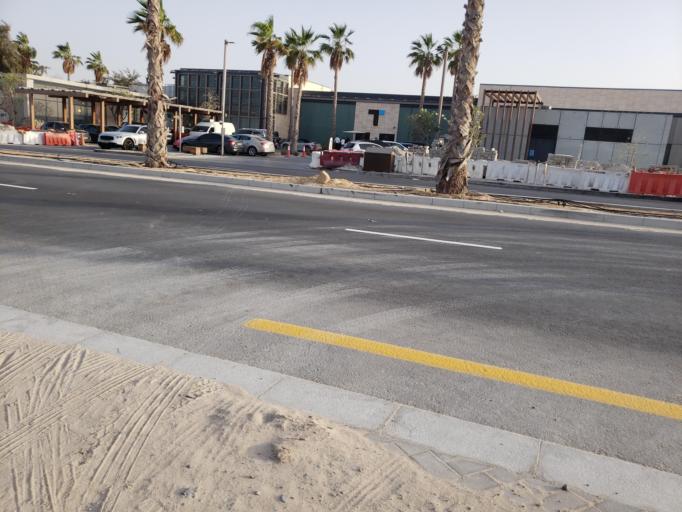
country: AE
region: Ash Shariqah
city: Sharjah
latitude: 25.2345
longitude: 55.2598
